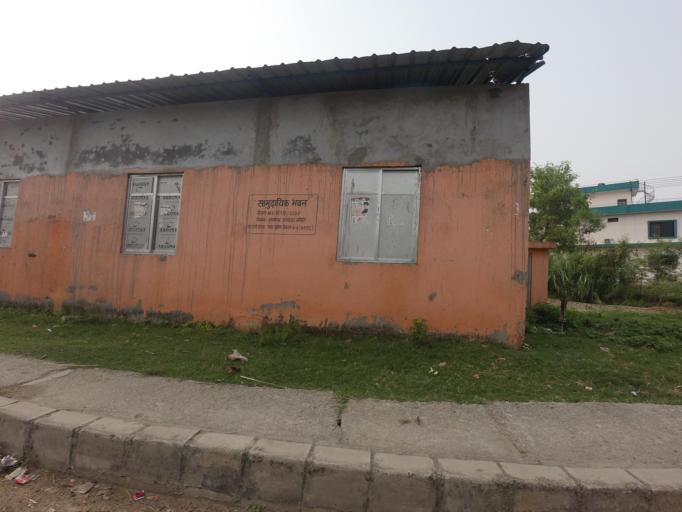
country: NP
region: Western Region
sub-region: Lumbini Zone
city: Bhairahawa
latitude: 27.4949
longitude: 83.4491
